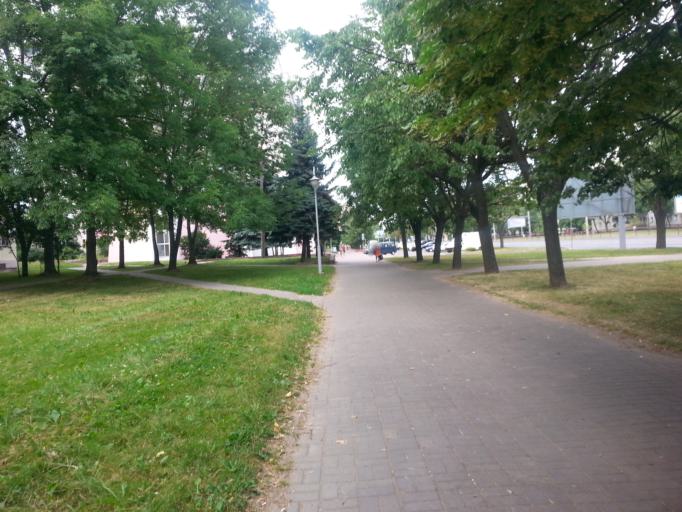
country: BY
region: Minsk
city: Novoye Medvezhino
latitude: 53.9119
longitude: 27.4947
